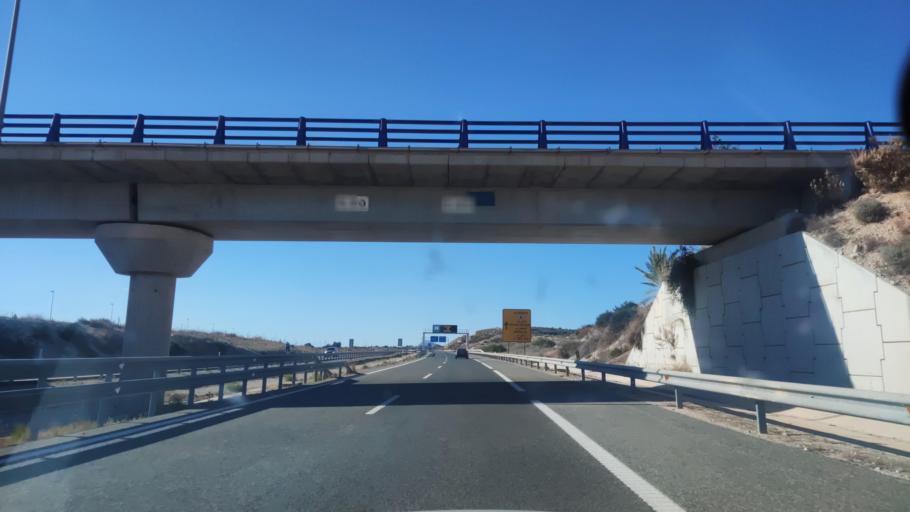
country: ES
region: Valencia
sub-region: Provincia de Alicante
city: el Campello
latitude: 38.4461
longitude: -0.3904
